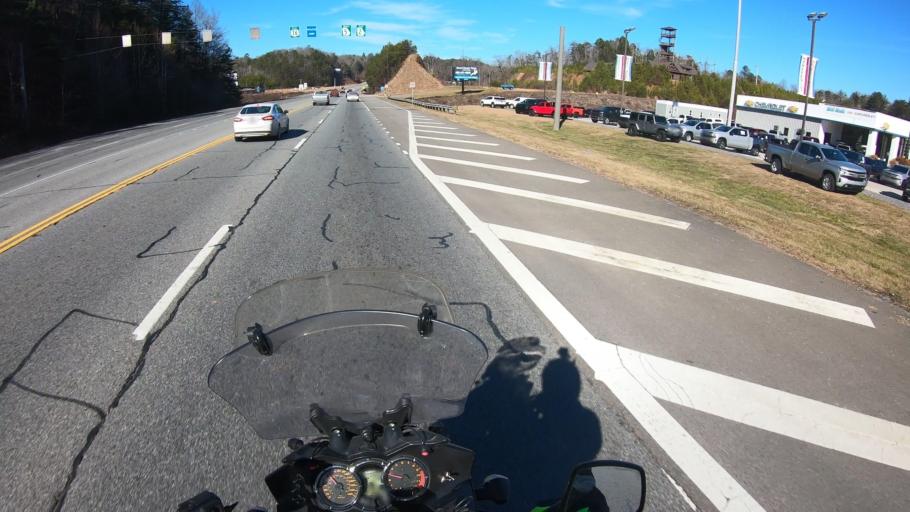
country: US
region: Georgia
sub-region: Fannin County
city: Blue Ridge
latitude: 34.8467
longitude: -84.3344
